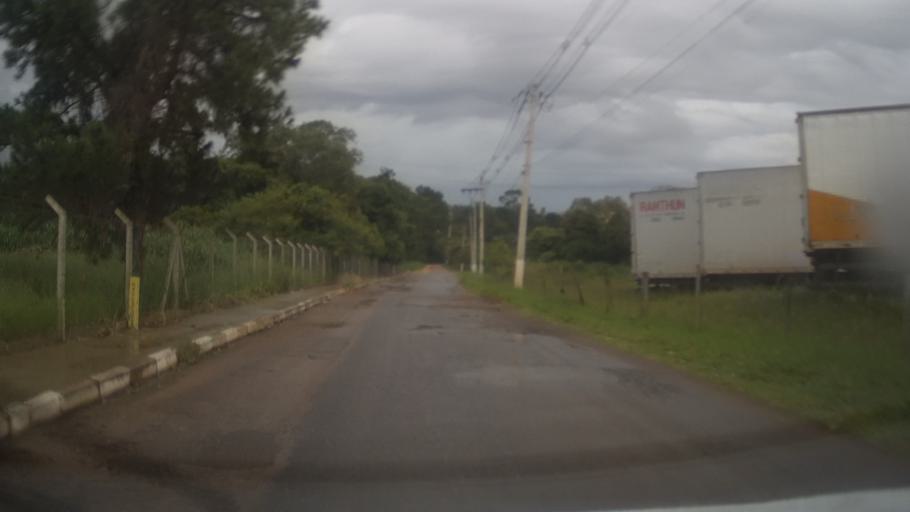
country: BR
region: Sao Paulo
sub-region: Itupeva
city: Itupeva
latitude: -23.1649
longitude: -47.0172
